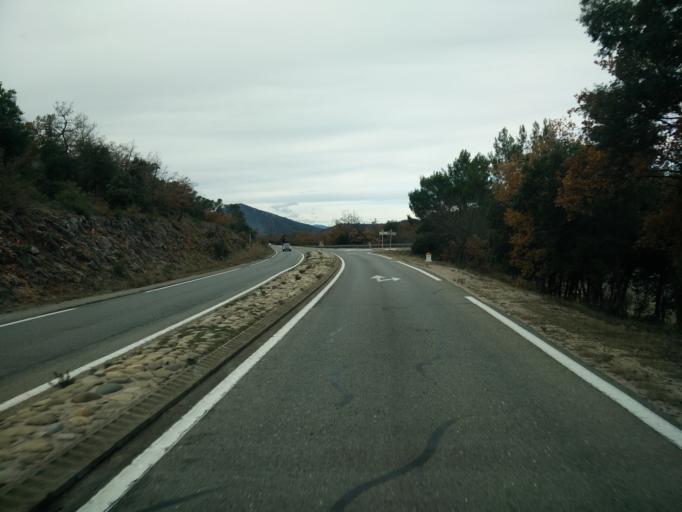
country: FR
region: Provence-Alpes-Cote d'Azur
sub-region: Departement du Var
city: Camps-la-Source
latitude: 43.3772
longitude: 6.0860
